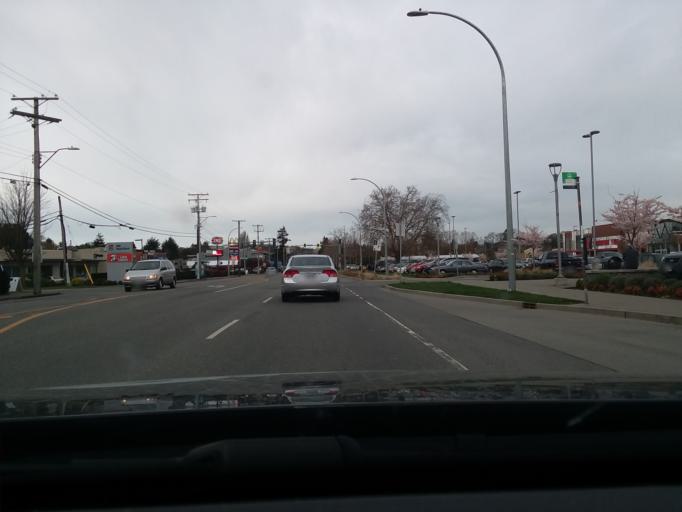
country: CA
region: British Columbia
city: Oak Bay
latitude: 48.4453
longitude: -123.3344
